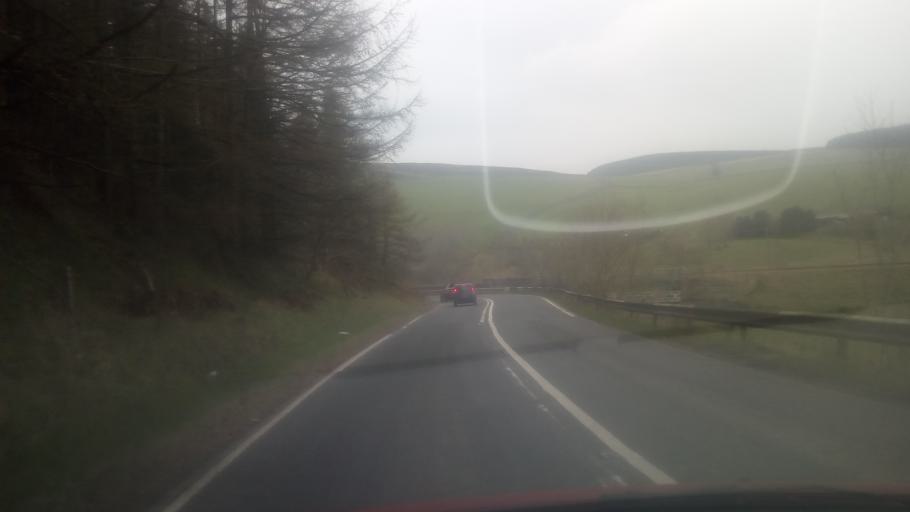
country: GB
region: Scotland
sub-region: The Scottish Borders
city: Galashiels
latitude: 55.7048
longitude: -2.8883
